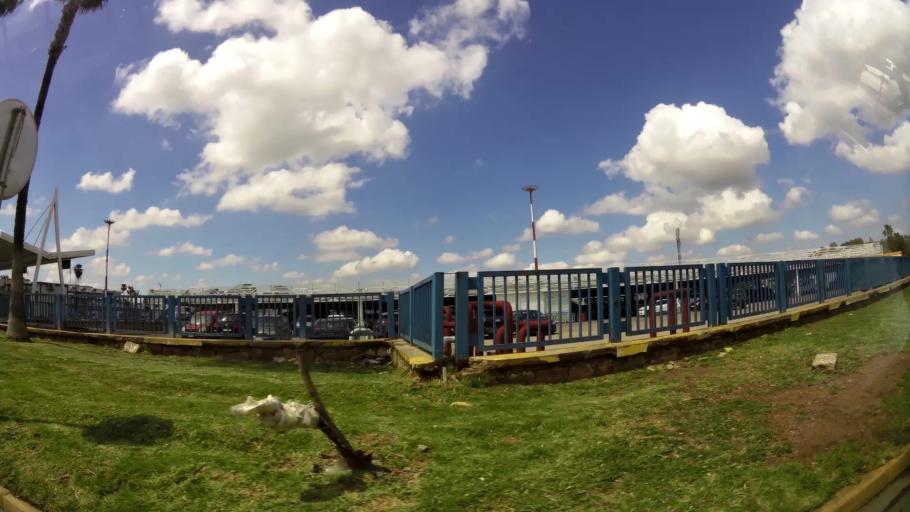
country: MA
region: Chaouia-Ouardigha
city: Nouaseur
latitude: 33.3745
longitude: -7.5790
